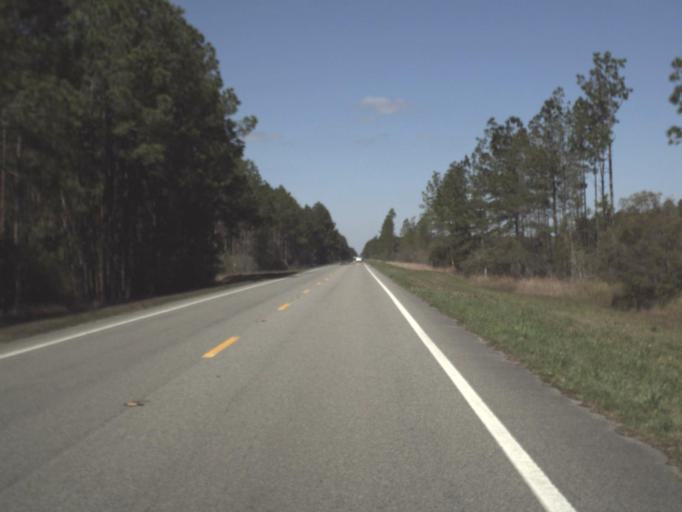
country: US
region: Florida
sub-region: Gulf County
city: Port Saint Joe
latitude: 29.9171
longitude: -85.2011
